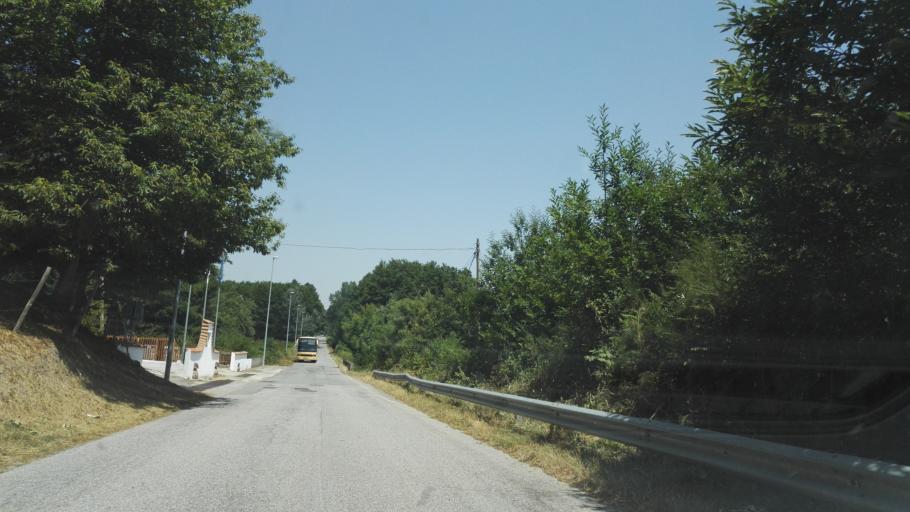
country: IT
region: Calabria
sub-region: Provincia di Vibo-Valentia
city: Mongiana
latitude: 38.5245
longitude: 16.3200
